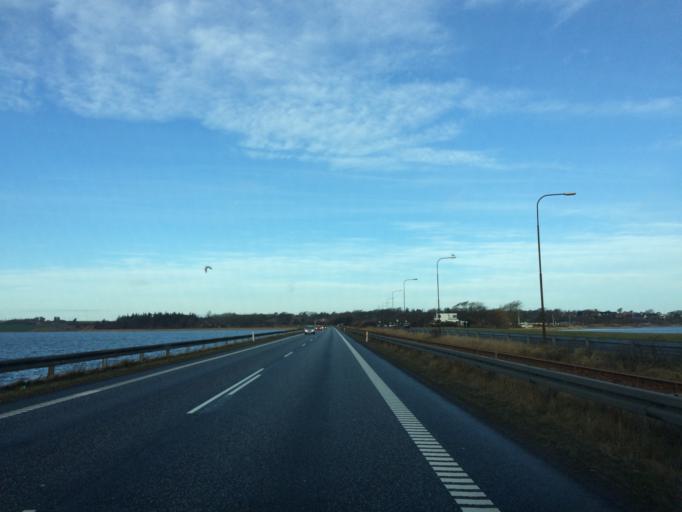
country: DK
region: Central Jutland
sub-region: Struer Kommune
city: Struer
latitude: 56.4976
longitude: 8.5827
